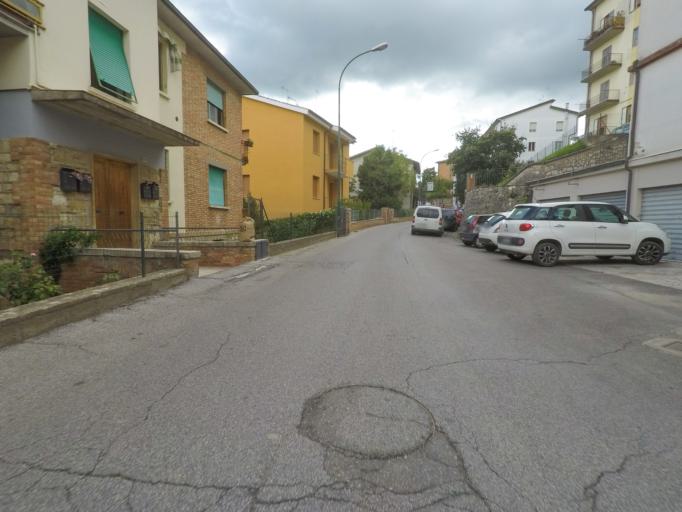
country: IT
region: Tuscany
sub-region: Provincia di Siena
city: Montepulciano
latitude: 43.0996
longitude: 11.7871
